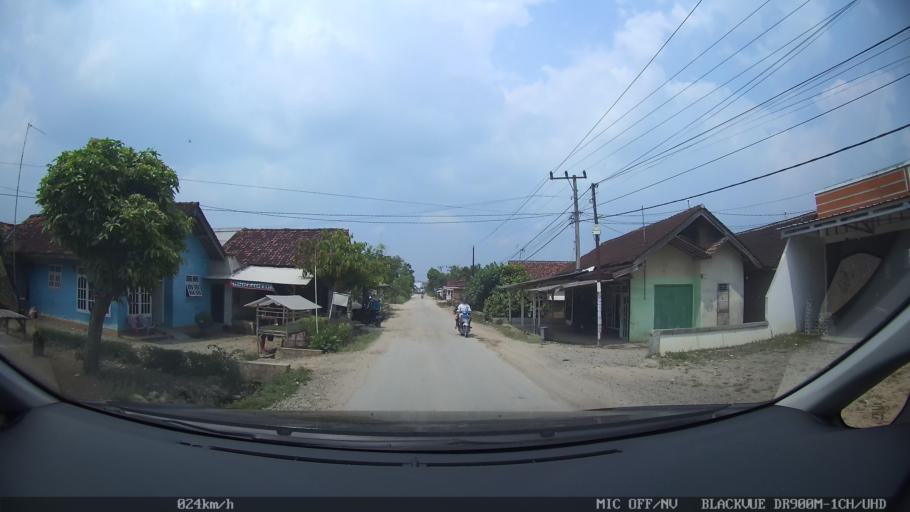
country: ID
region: Lampung
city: Gadingrejo
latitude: -5.3777
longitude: 105.0521
